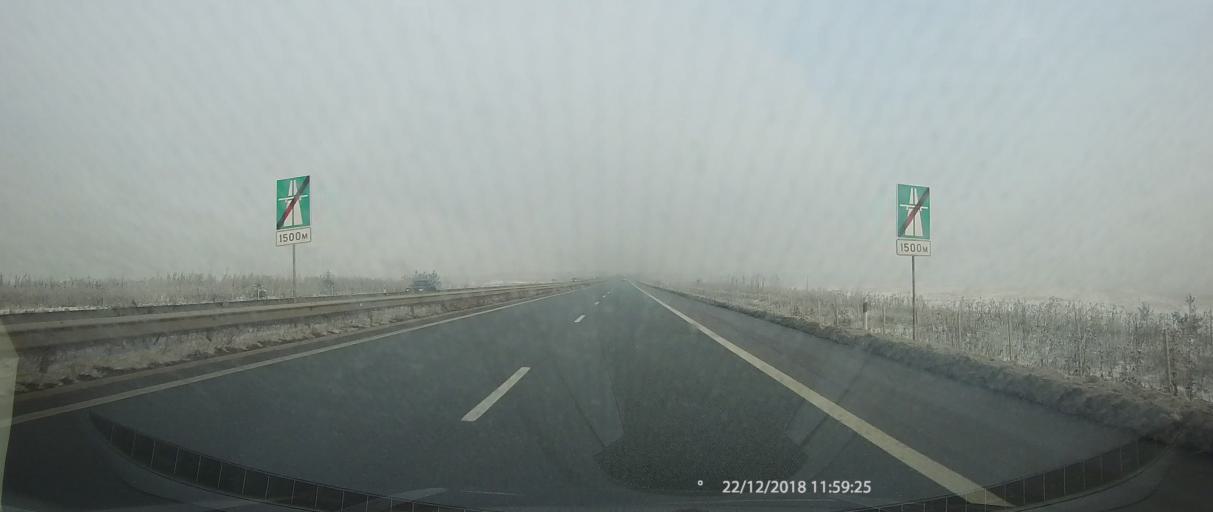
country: BG
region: Sofiya
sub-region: Obshtina Bozhurishte
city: Bozhurishte
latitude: 42.7028
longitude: 23.2099
